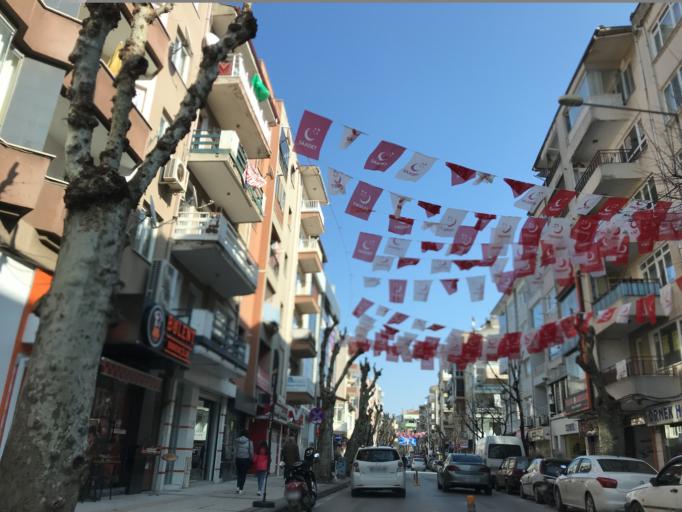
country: TR
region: Yalova
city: Yalova
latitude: 40.6558
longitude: 29.2712
